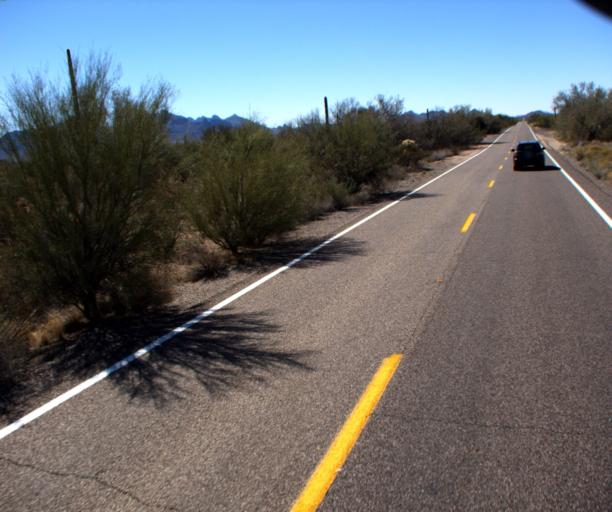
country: US
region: Arizona
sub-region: Pima County
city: Ajo
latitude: 32.1651
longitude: -112.7636
